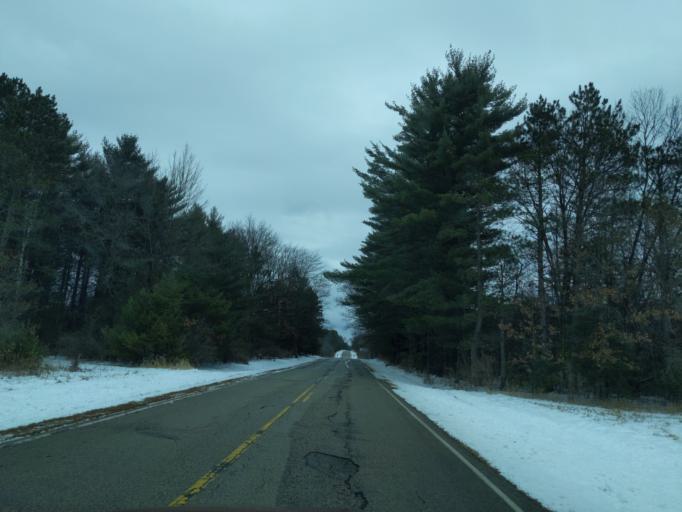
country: US
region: Wisconsin
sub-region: Marquette County
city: Montello
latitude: 43.9197
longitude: -89.3227
